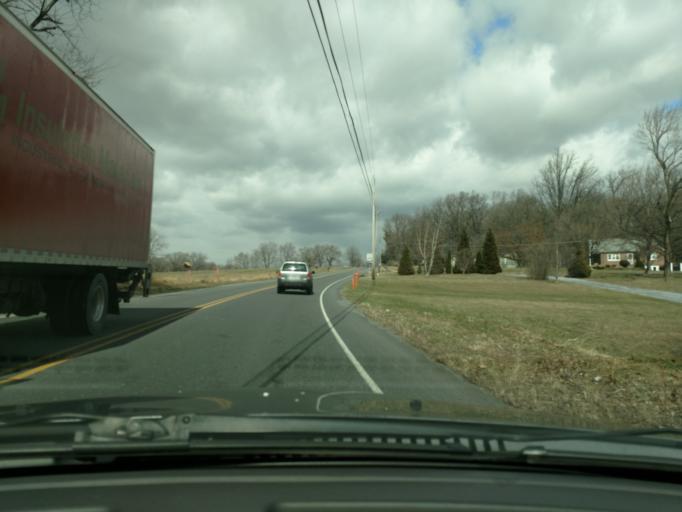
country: US
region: Pennsylvania
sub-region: Lebanon County
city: Myerstown
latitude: 40.4028
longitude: -76.3044
